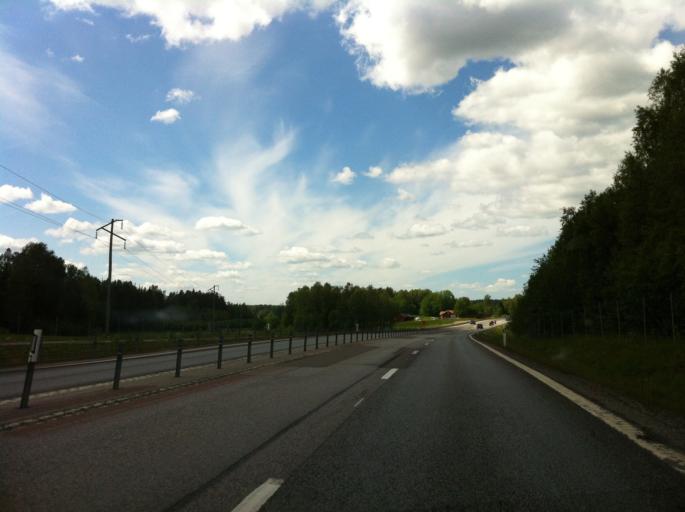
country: SE
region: Vaestra Goetaland
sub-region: Amals Kommun
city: Amal
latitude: 59.0912
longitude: 12.7250
